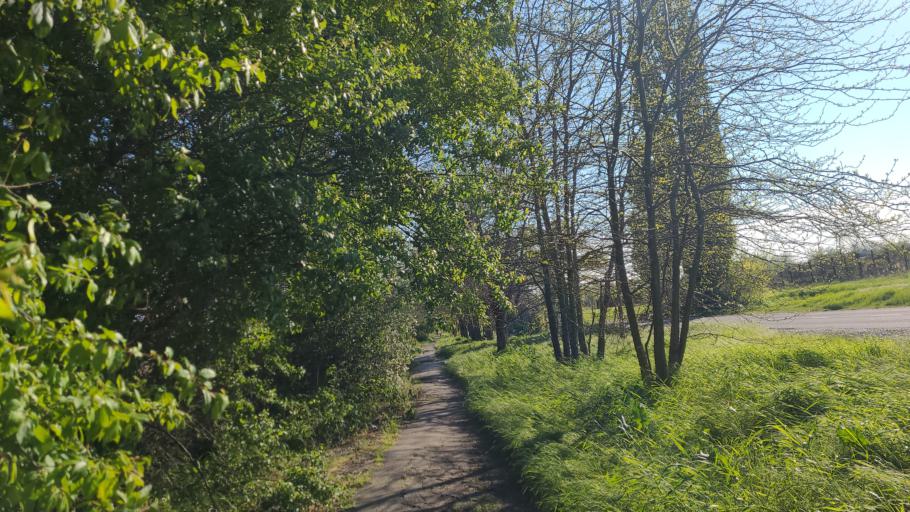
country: RU
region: Krasnodarskiy
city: Tsibanobalka
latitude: 44.9500
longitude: 37.3115
